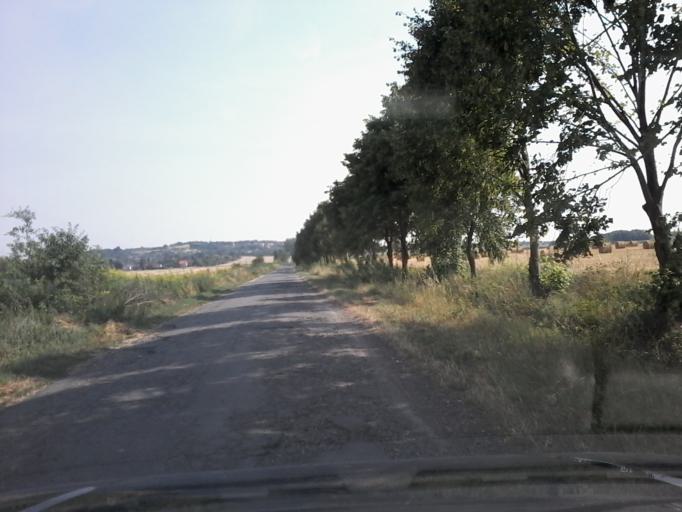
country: HU
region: Vas
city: Janoshaza
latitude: 47.1702
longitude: 17.0910
